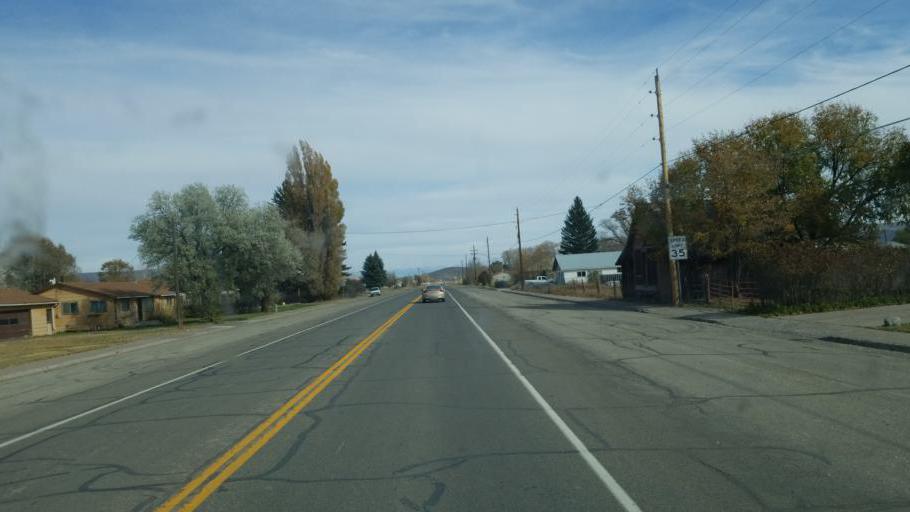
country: US
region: Colorado
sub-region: Conejos County
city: Conejos
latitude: 37.1738
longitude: -105.9327
